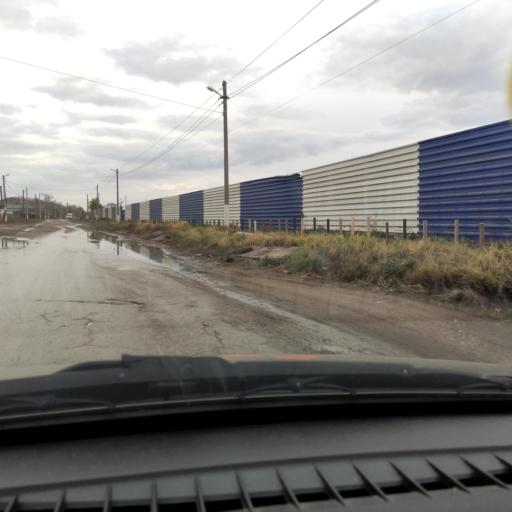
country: RU
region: Samara
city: Podstepki
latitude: 53.5153
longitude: 49.2183
